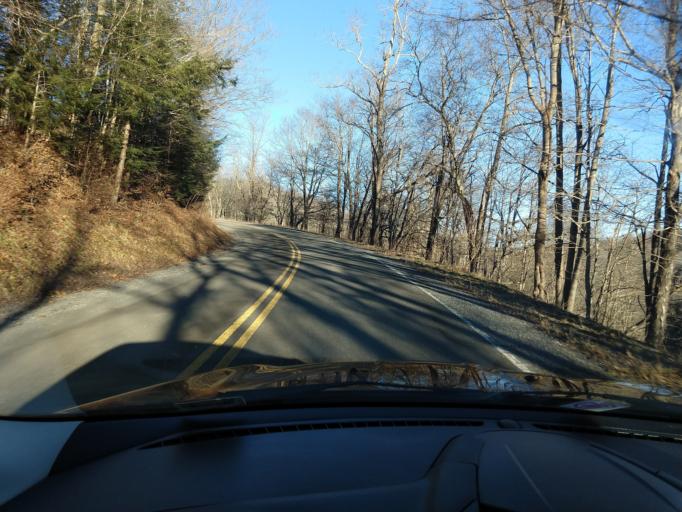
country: US
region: Virginia
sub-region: Highland County
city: Monterey
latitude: 38.4639
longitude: -79.6806
